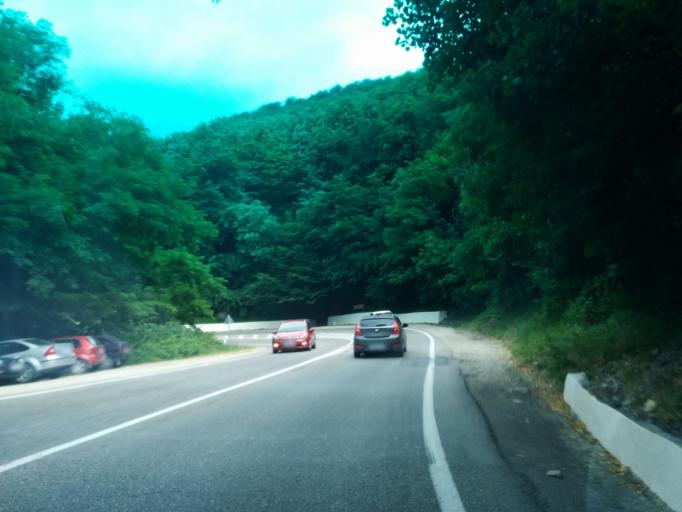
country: RU
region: Krasnodarskiy
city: Nebug
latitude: 44.1738
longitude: 38.9699
